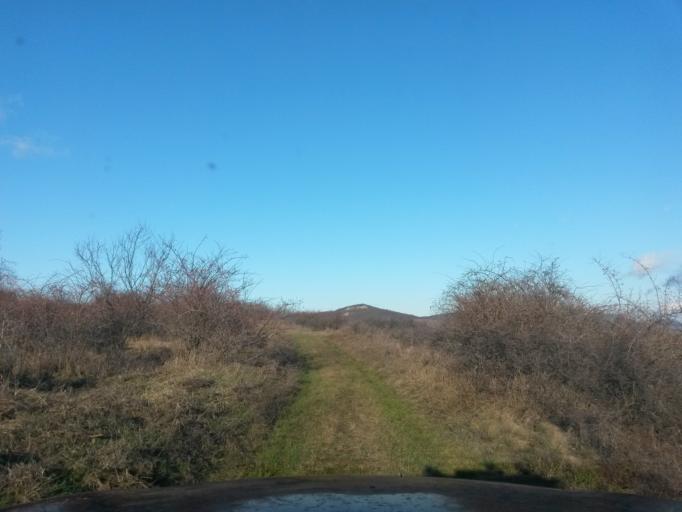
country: HU
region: Borsod-Abauj-Zemplen
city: Sarospatak
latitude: 48.3252
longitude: 21.5379
